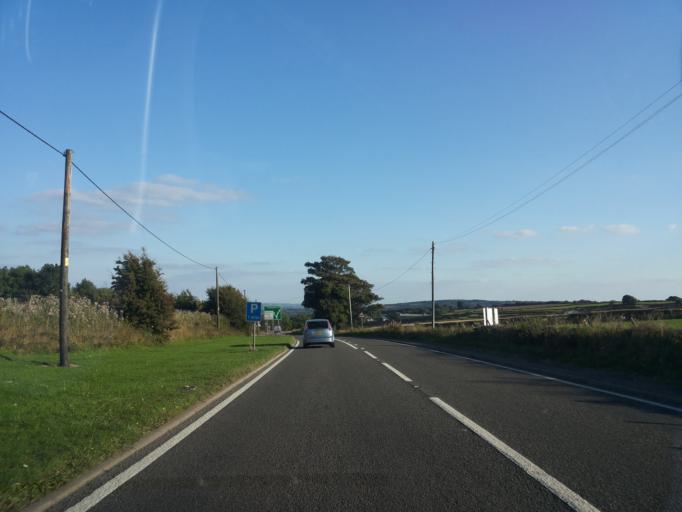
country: GB
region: England
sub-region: Derbyshire
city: Dronfield
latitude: 53.2358
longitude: -1.5347
